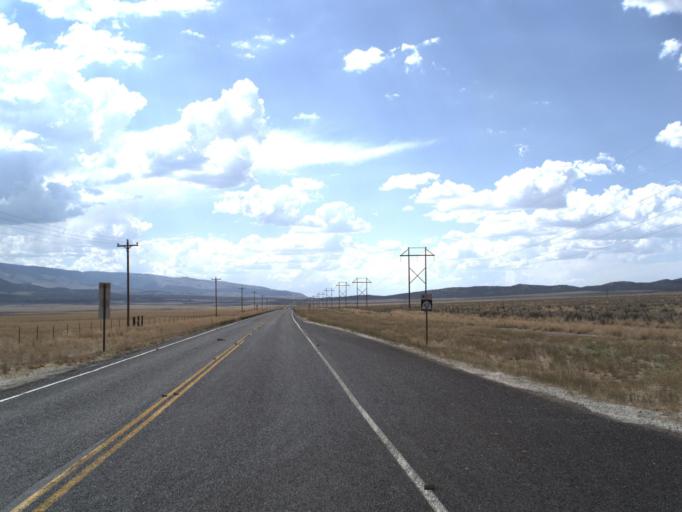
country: US
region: Idaho
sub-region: Oneida County
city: Malad City
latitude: 41.9653
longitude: -113.0577
